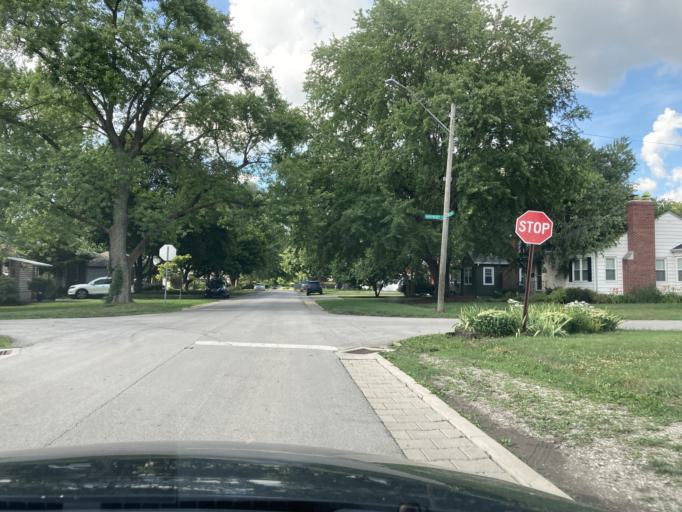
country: US
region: Indiana
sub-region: Marion County
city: Broad Ripple
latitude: 39.8603
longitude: -86.1339
